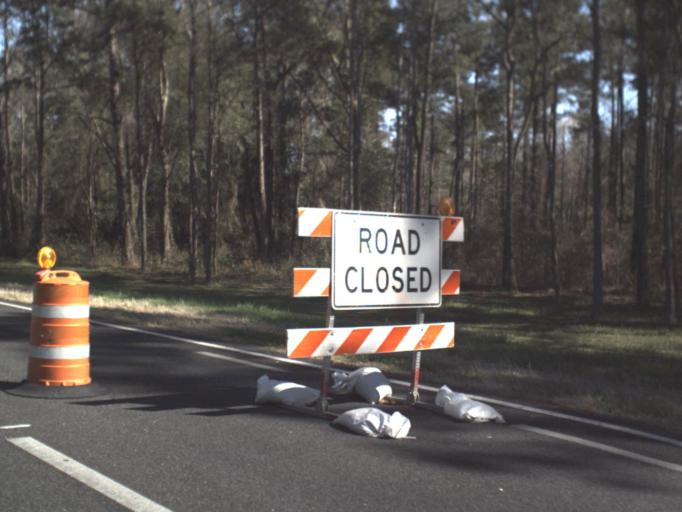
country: US
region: Florida
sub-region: Gadsden County
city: Quincy
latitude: 30.5542
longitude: -84.5221
